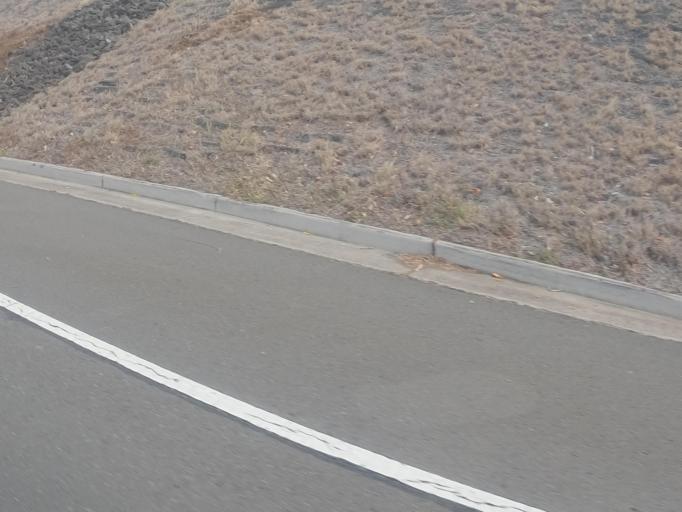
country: US
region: Hawaii
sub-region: Honolulu County
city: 'Aiea
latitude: 21.3759
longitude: -157.9305
